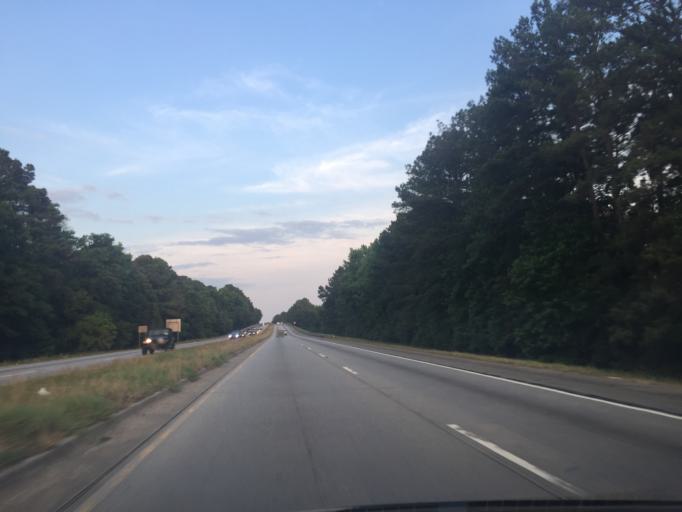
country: US
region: Georgia
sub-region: Chatham County
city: Savannah
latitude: 32.0379
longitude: -81.1401
